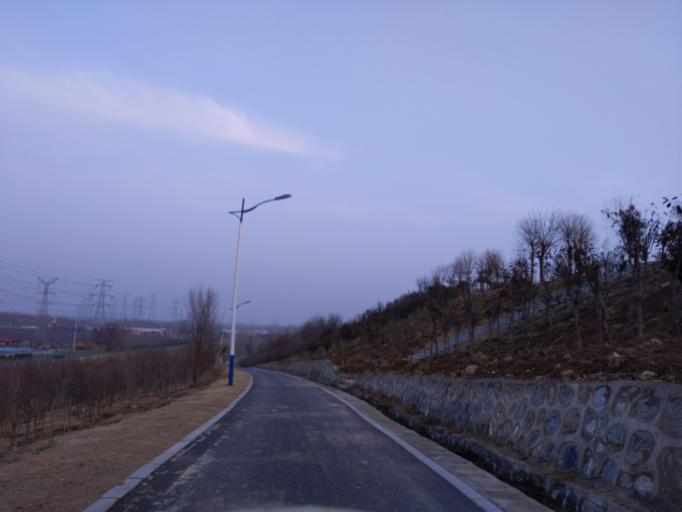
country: CN
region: Henan Sheng
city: Zhongyuanlu
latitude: 35.8160
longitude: 115.0577
